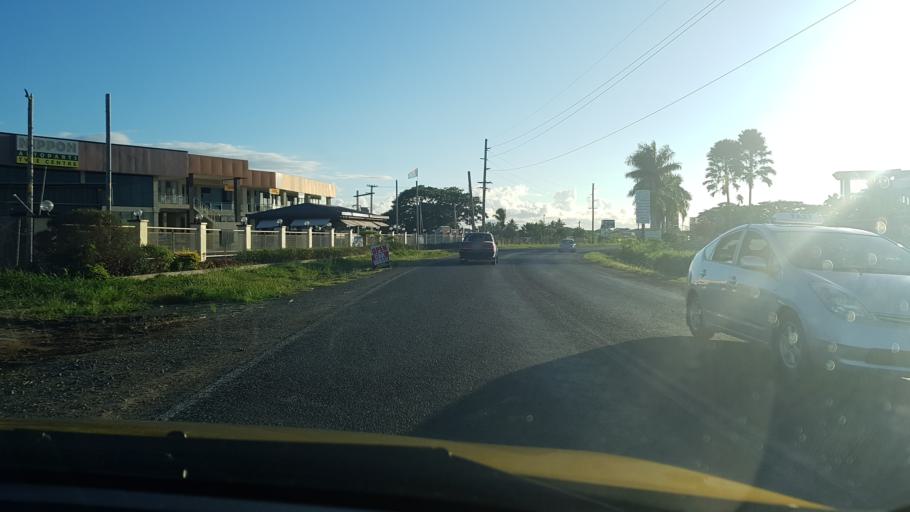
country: FJ
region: Western
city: Nadi
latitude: -17.7789
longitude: 177.4542
